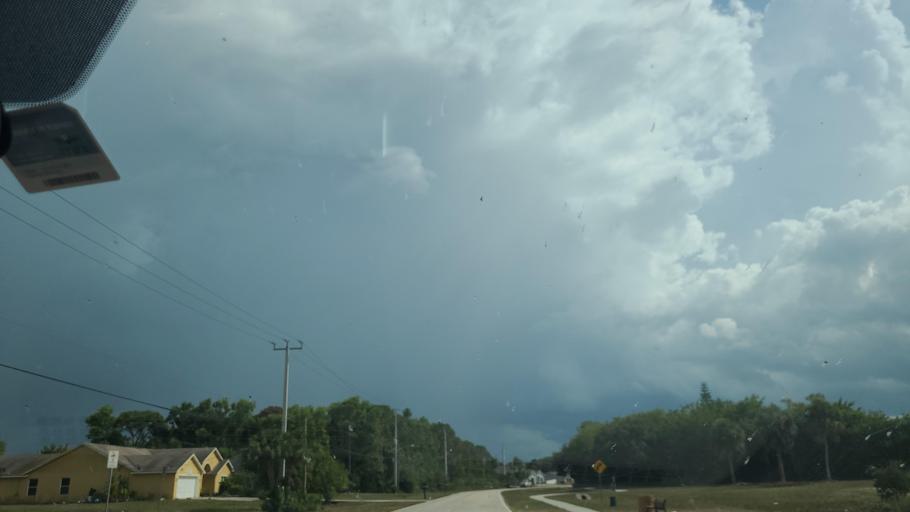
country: US
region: Florida
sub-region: Saint Lucie County
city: Port Saint Lucie
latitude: 27.2487
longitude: -80.3545
